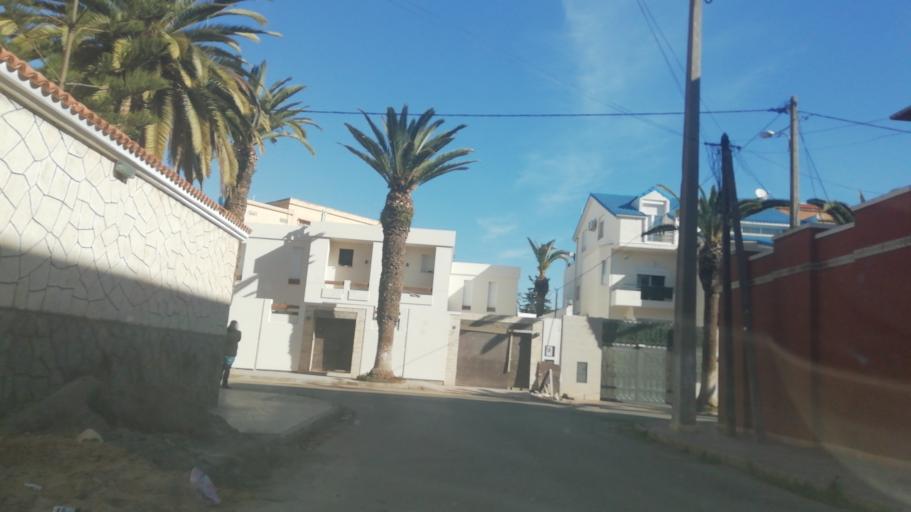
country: DZ
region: Oran
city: Oran
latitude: 35.6746
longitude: -0.6440
